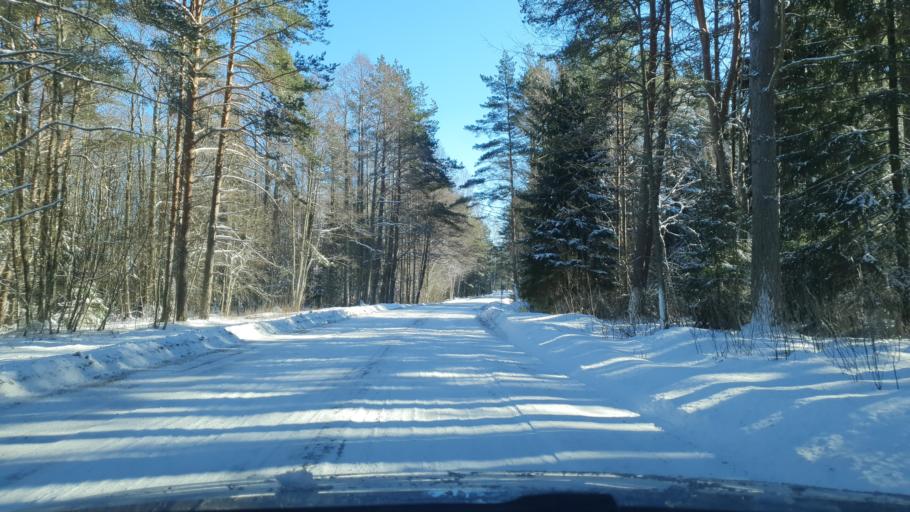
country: EE
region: Laeaene-Virumaa
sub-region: Haljala vald
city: Haljala
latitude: 59.6050
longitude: 26.0554
